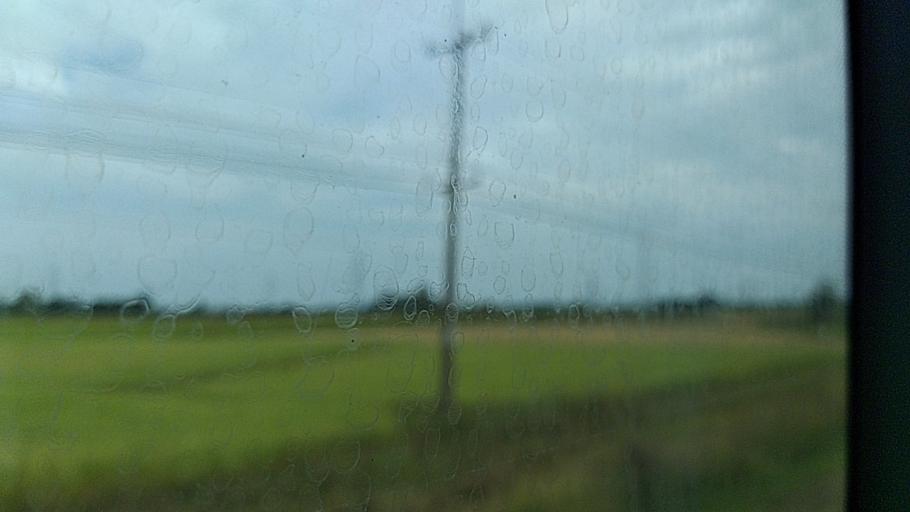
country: TH
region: Roi Et
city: Si Somdet
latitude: 16.1264
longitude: 103.4731
